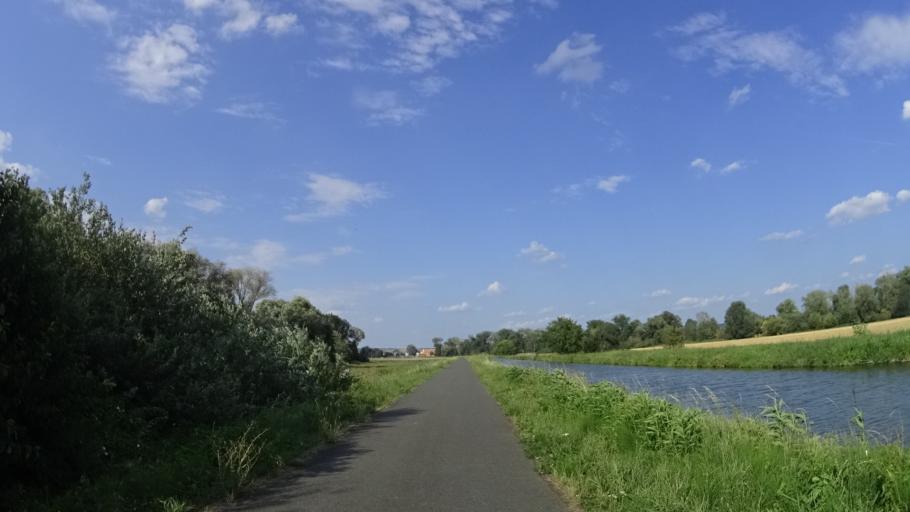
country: CZ
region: Zlin
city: Babice
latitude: 49.1264
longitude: 17.4944
